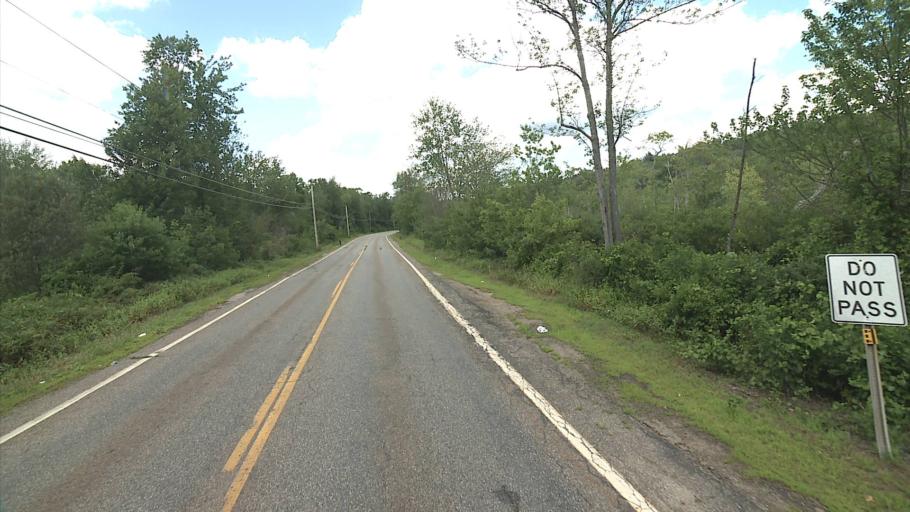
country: US
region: Connecticut
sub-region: Tolland County
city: Stafford
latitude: 41.9312
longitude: -72.1935
